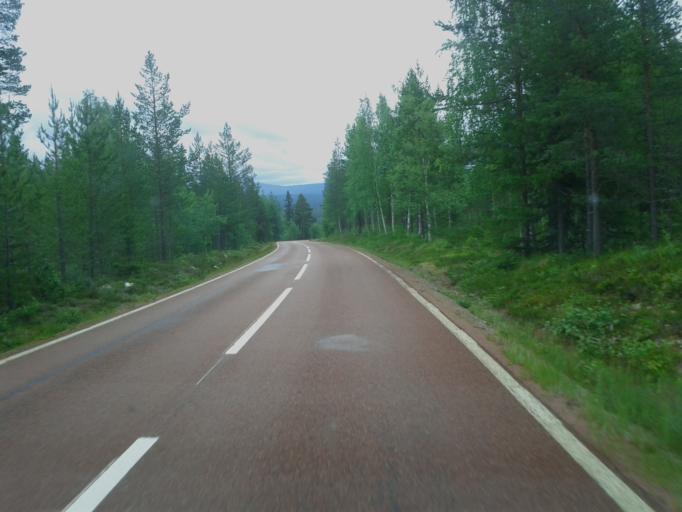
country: NO
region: Hedmark
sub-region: Trysil
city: Innbygda
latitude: 61.8523
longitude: 12.6201
